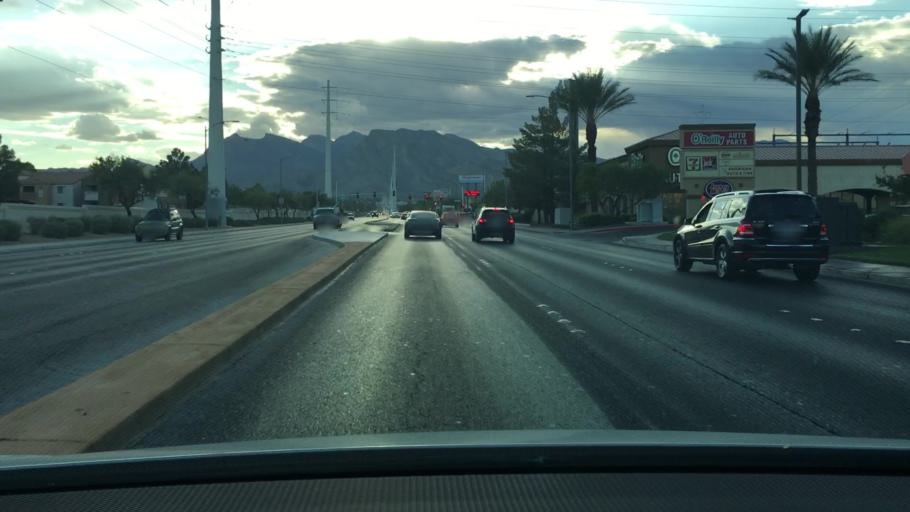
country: US
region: Nevada
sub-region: Clark County
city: Spring Valley
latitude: 36.2187
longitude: -115.2761
